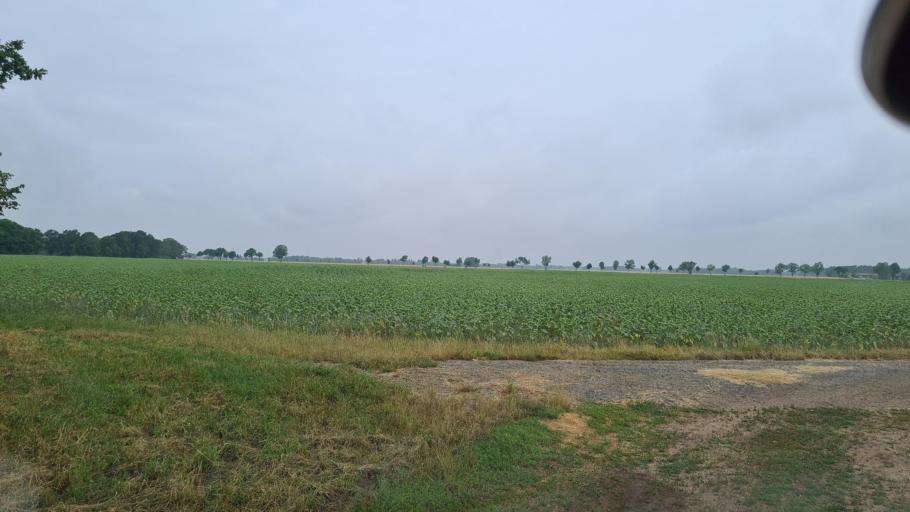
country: DE
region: Brandenburg
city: Herzberg
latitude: 51.7310
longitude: 13.2017
